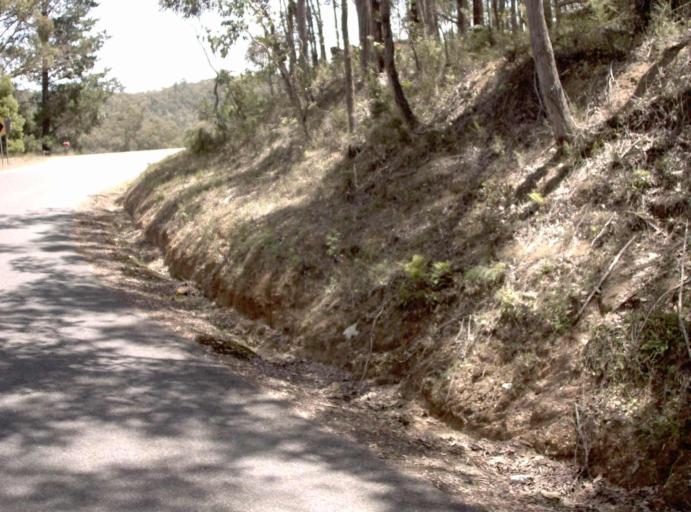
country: AU
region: New South Wales
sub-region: Bombala
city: Bombala
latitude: -37.5401
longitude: 148.9328
